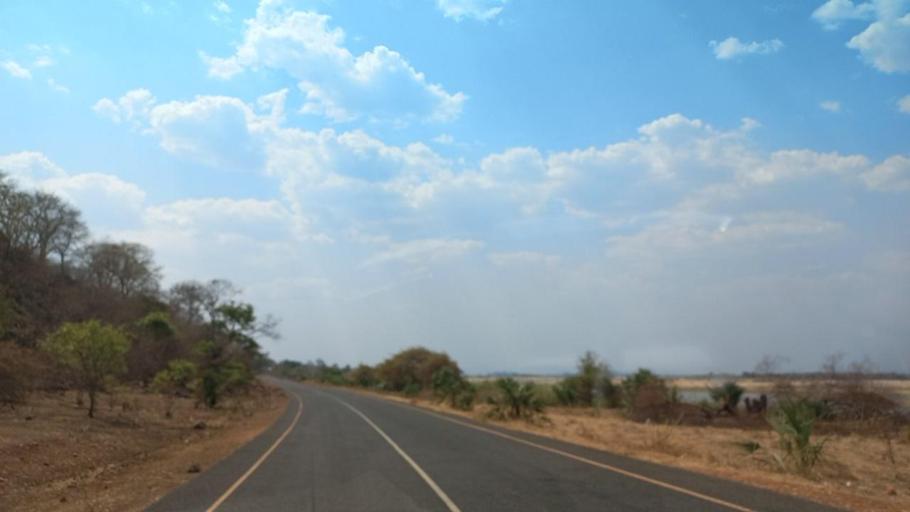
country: ZM
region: Lusaka
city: Luangwa
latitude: -15.3130
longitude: 30.3283
